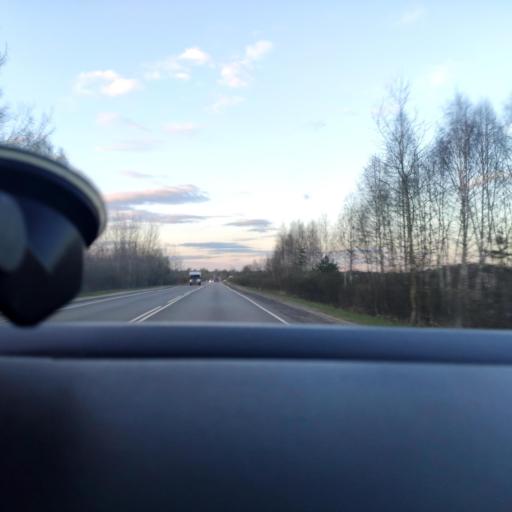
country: RU
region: Moskovskaya
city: Krasnyy Tkach
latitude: 55.4198
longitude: 39.1825
